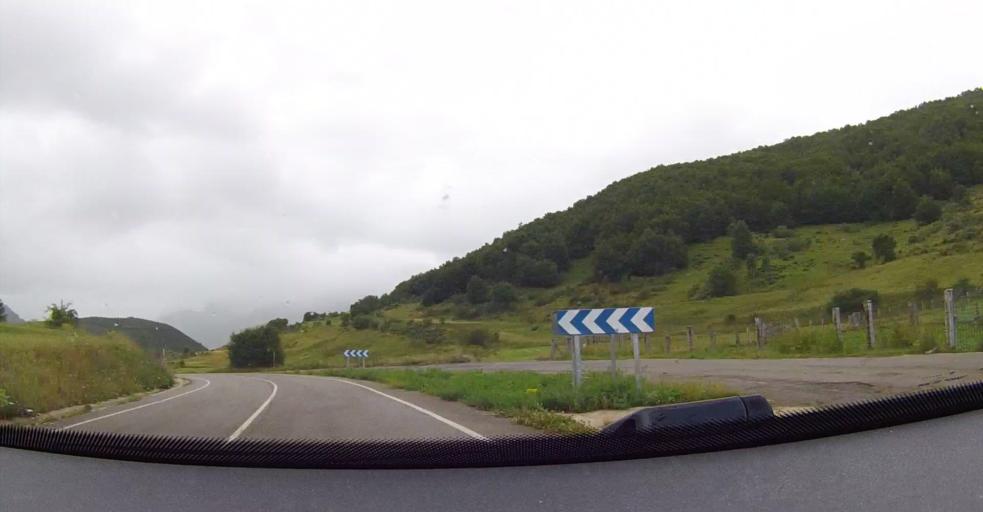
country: ES
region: Castille and Leon
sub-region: Provincia de Leon
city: Acebedo
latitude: 43.0613
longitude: -5.1383
